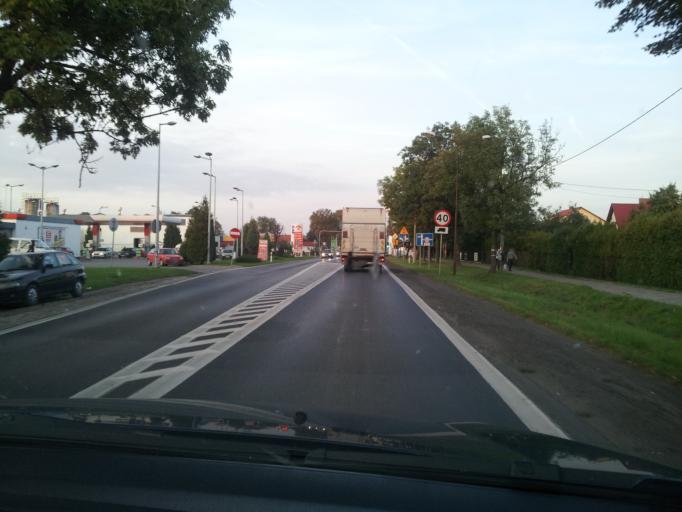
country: PL
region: Kujawsko-Pomorskie
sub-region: Powiat inowroclawski
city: Gniewkowo
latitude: 52.8921
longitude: 18.4014
